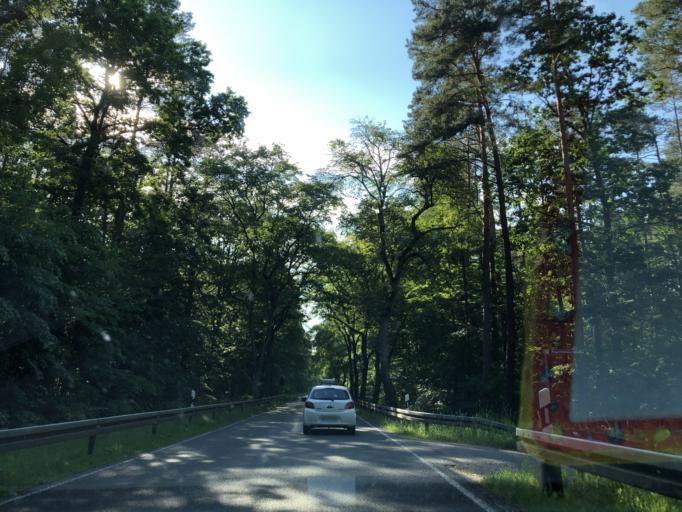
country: DE
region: Brandenburg
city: Joachimsthal
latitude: 52.9677
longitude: 13.7682
